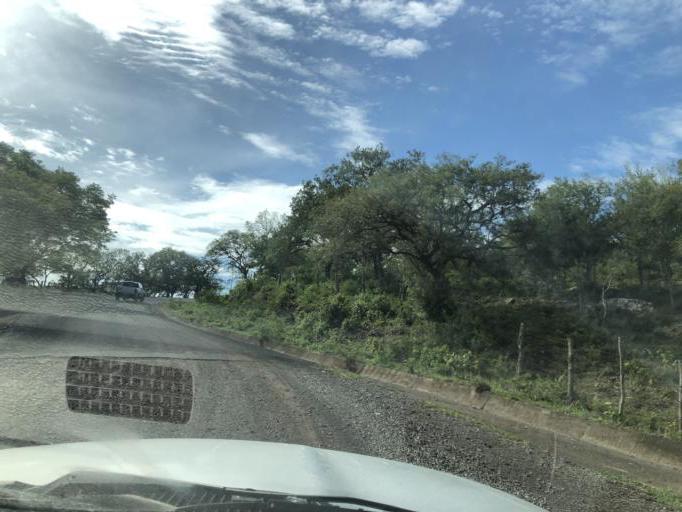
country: MX
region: Veracruz
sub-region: Alto Lucero de Gutierrez Barrios
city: Palma Sola
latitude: 19.7828
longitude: -96.5548
